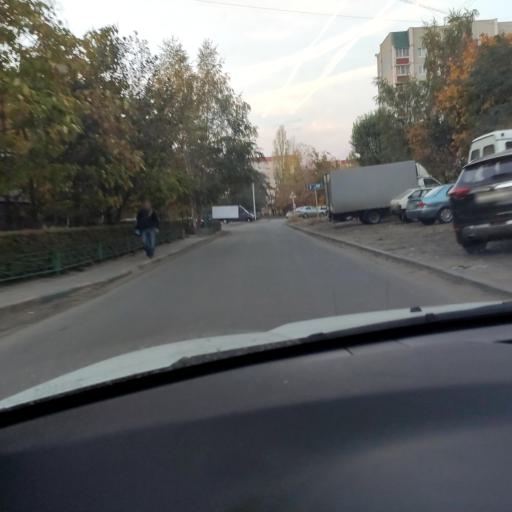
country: RU
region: Voronezj
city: Podgornoye
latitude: 51.7184
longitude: 39.1710
